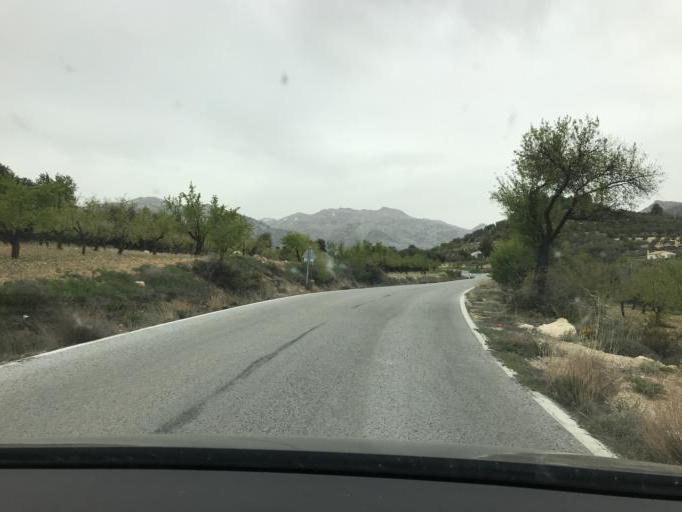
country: ES
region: Andalusia
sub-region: Provincia de Granada
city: Castril
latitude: 37.8104
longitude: -2.7658
